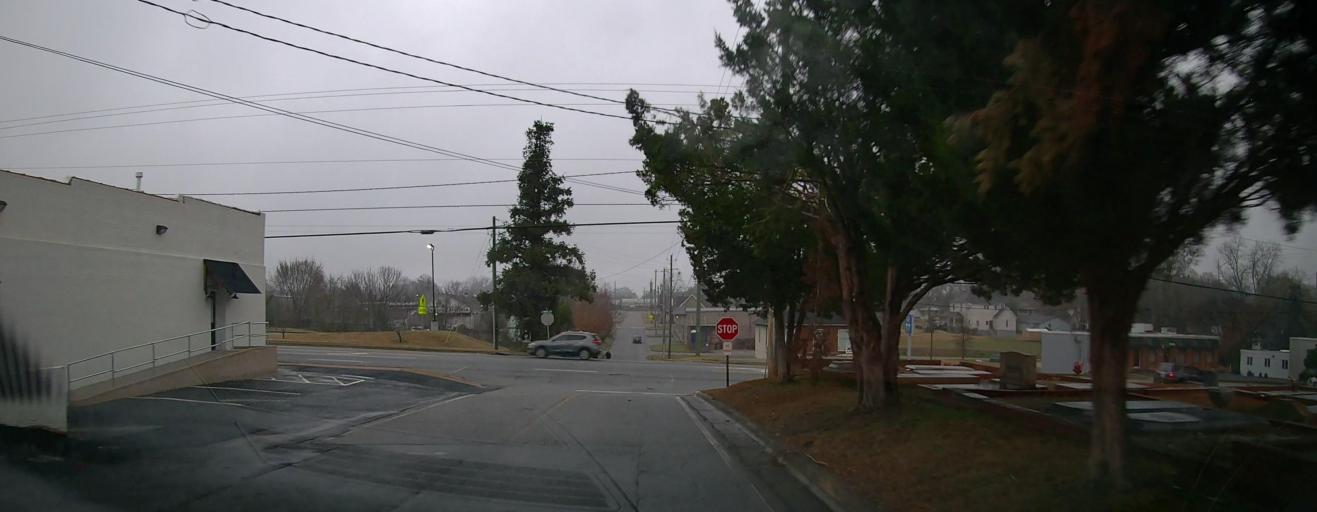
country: US
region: Georgia
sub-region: Spalding County
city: Griffin
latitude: 33.2466
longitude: -84.2573
